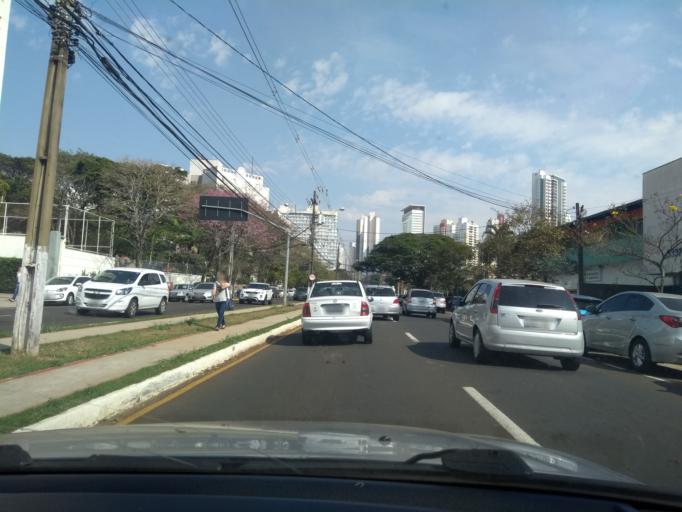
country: BR
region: Parana
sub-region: Londrina
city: Londrina
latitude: -23.3350
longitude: -51.1685
